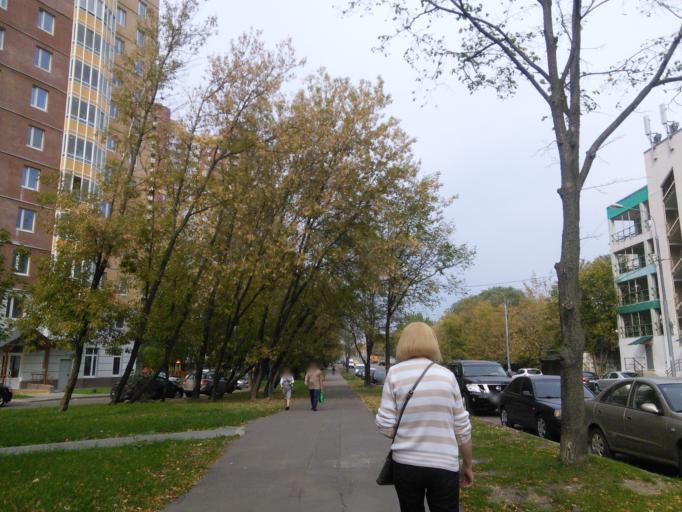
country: RU
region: Moskovskaya
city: Levoberezhnaya
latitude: 55.8675
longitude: 37.4745
